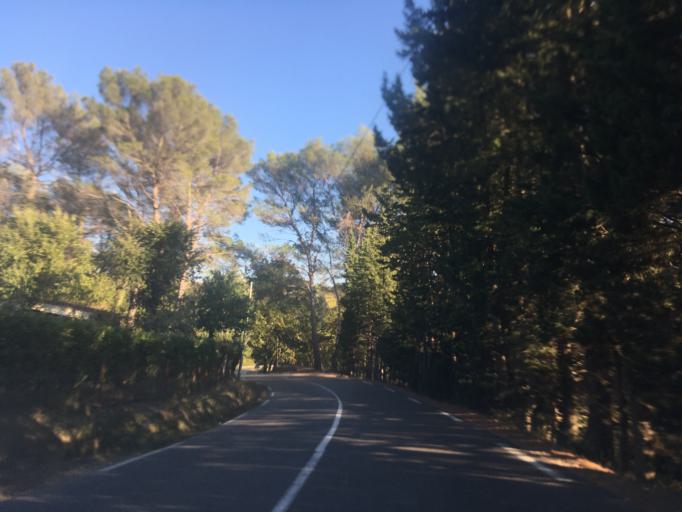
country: FR
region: Provence-Alpes-Cote d'Azur
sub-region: Departement du Var
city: Villecroze
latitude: 43.5689
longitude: 6.2861
